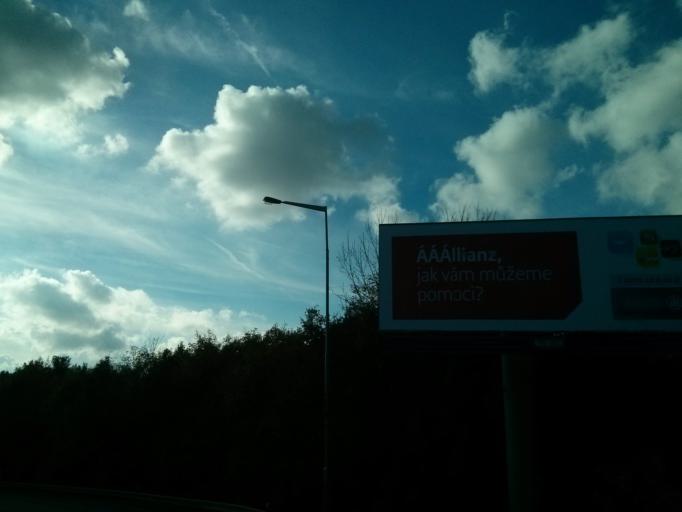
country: CZ
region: Praha
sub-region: Praha 1
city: Mala Strana
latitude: 50.0569
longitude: 14.3379
